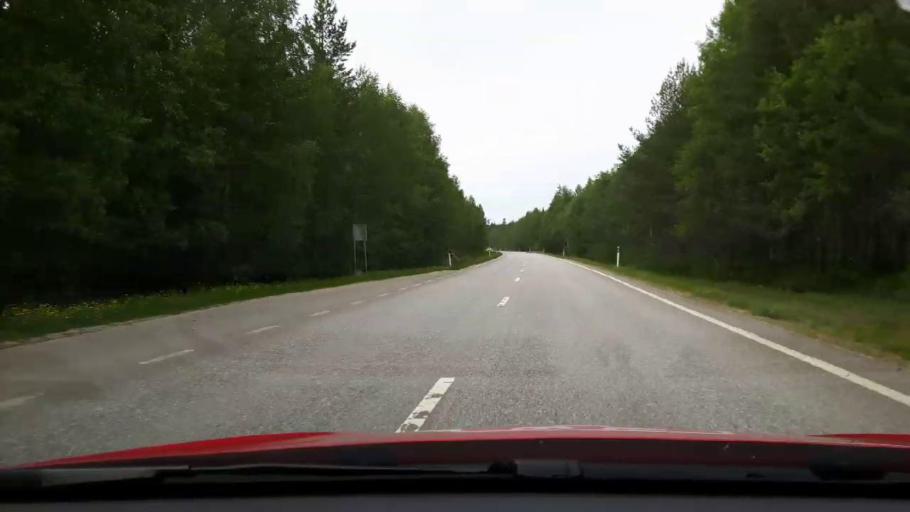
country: SE
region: Jaemtland
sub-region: Harjedalens Kommun
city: Sveg
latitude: 62.0969
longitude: 14.2312
